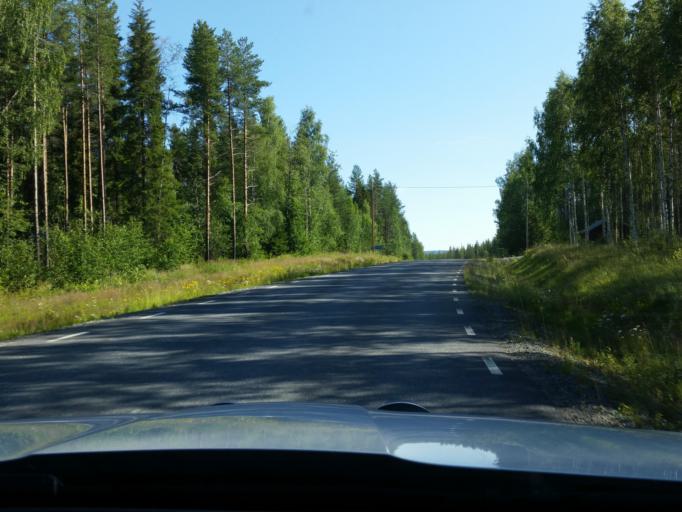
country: SE
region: Norrbotten
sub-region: Alvsbyns Kommun
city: AElvsbyn
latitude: 65.6022
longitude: 20.8715
